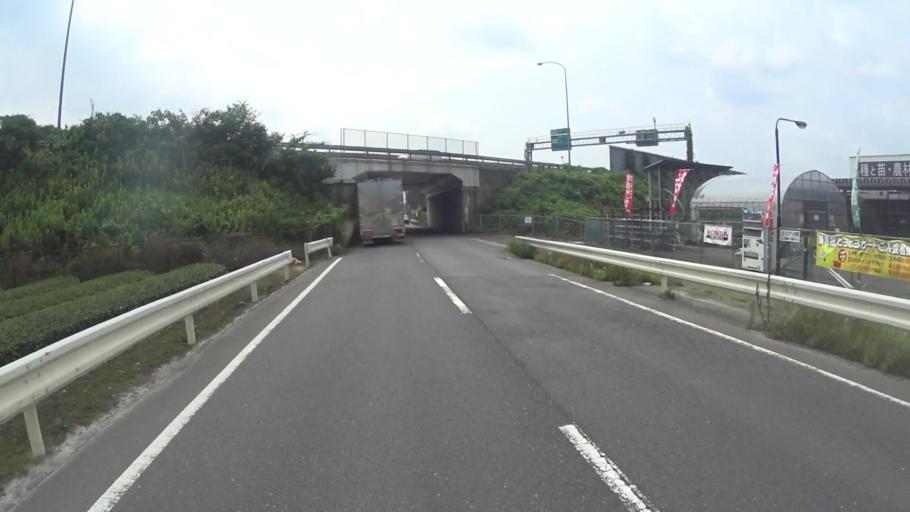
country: JP
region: Mie
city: Komono
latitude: 34.9296
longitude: 136.4875
